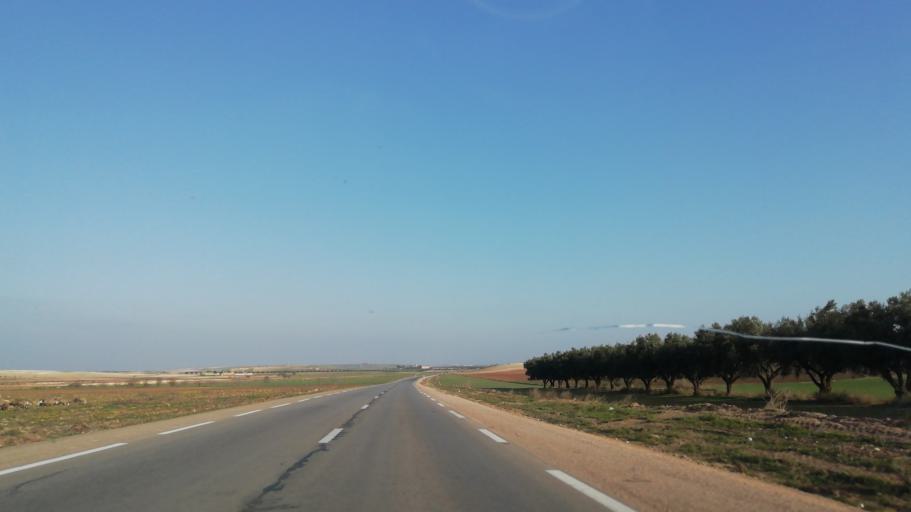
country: DZ
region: Sidi Bel Abbes
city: Sidi Bel Abbes
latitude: 35.1789
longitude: -0.8025
